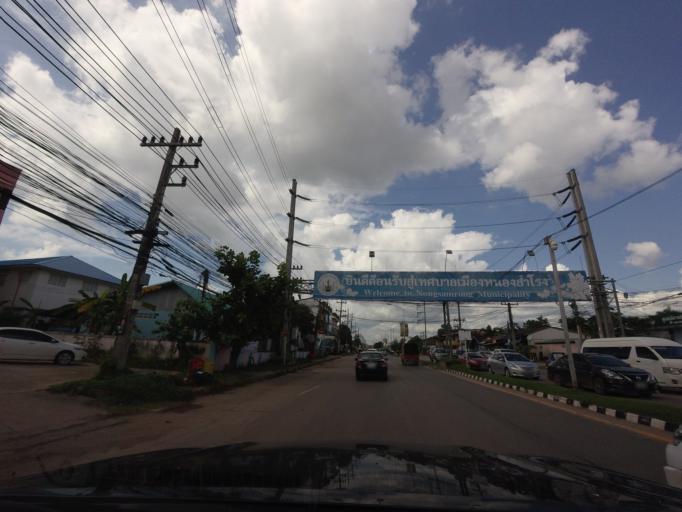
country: TH
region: Changwat Udon Thani
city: Udon Thani
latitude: 17.4260
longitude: 102.7770
